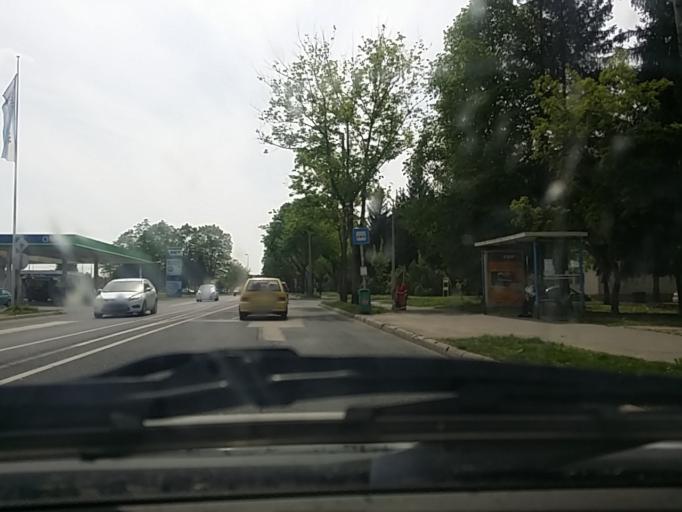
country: HU
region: Zala
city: Nagykanizsa
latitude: 46.4567
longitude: 17.0096
